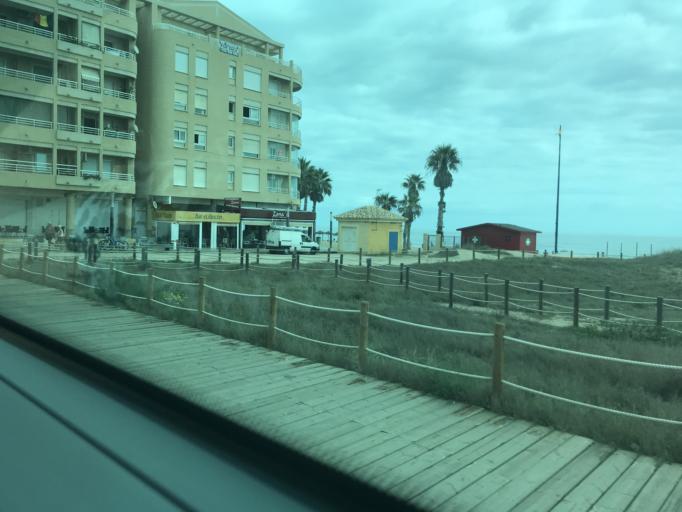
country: ES
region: Valencia
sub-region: Provincia de Alicante
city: Torrevieja
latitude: 38.0245
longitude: -0.6542
